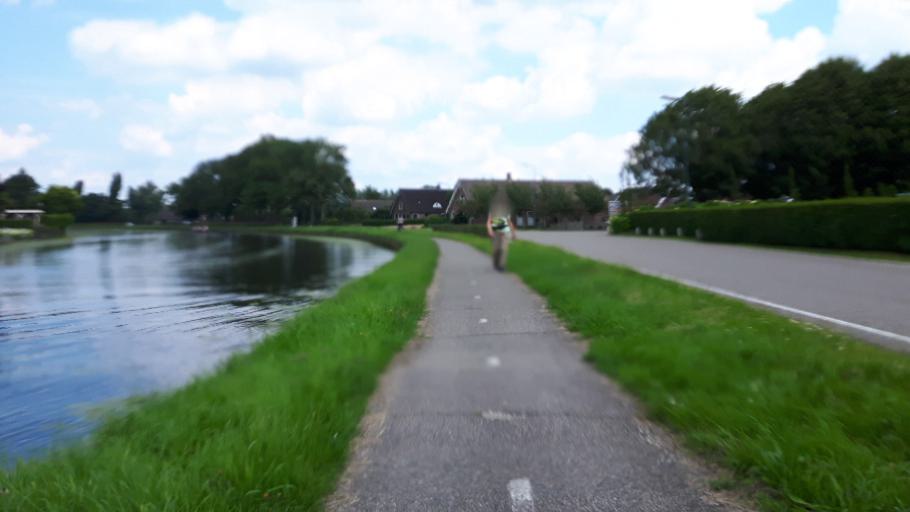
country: NL
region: Utrecht
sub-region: Gemeente Woerden
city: Woerden
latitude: 52.0776
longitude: 4.8314
